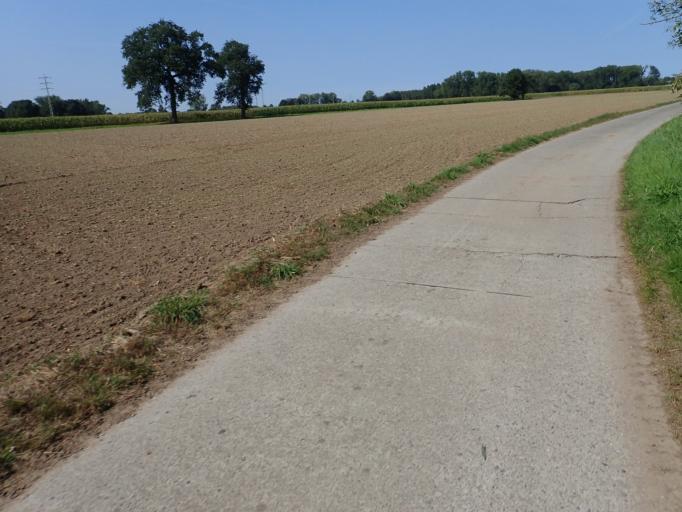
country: BE
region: Flanders
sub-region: Provincie Oost-Vlaanderen
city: Buggenhout
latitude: 51.0254
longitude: 4.2115
